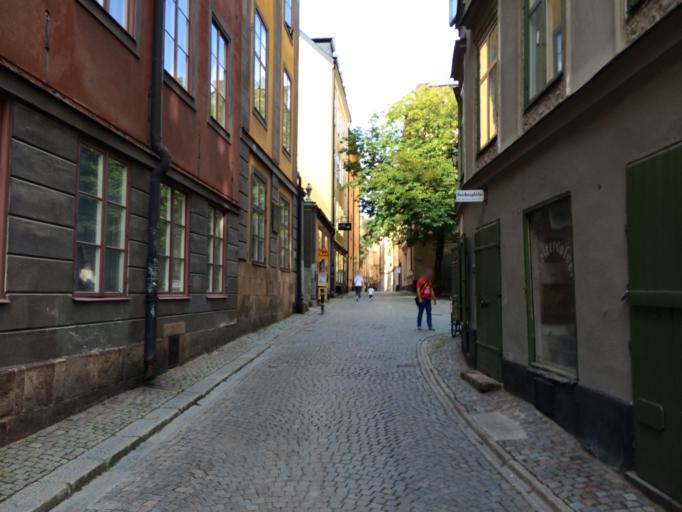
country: SE
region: Stockholm
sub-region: Stockholms Kommun
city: Stockholm
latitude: 59.3236
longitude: 18.0731
